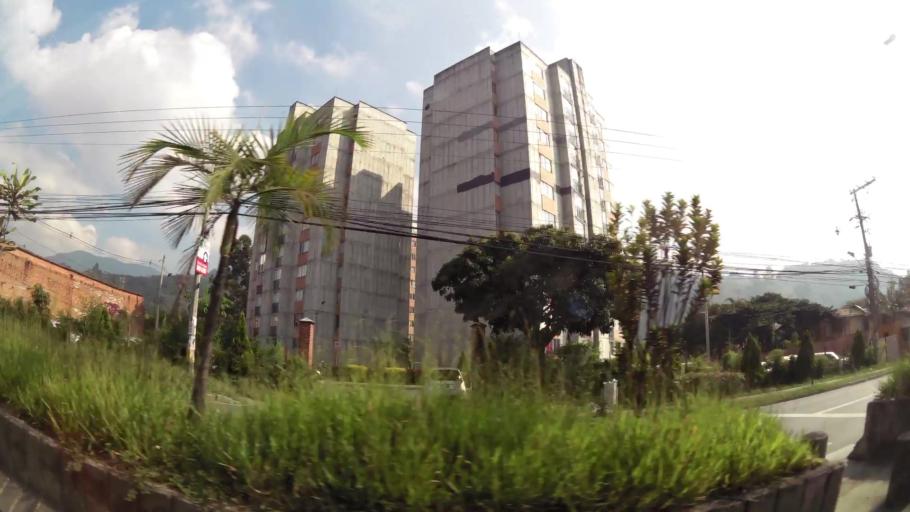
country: CO
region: Antioquia
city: La Estrella
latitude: 6.1724
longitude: -75.6295
